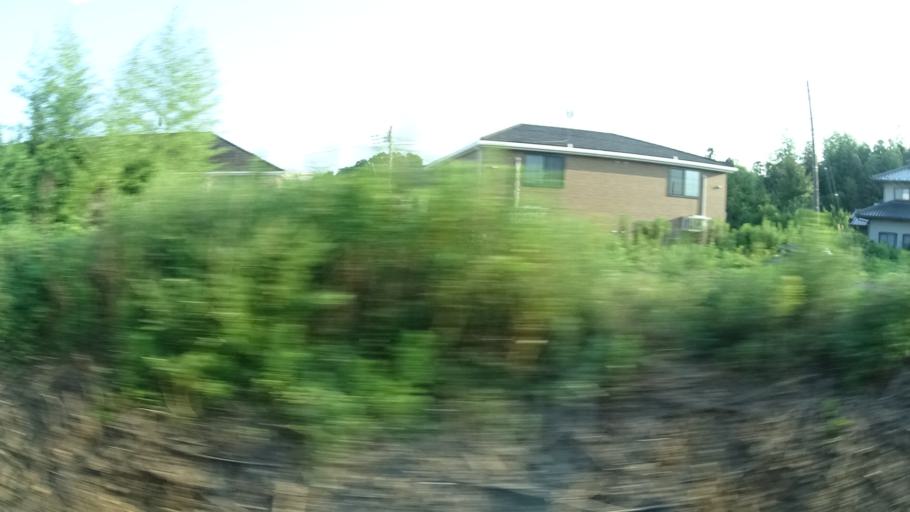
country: JP
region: Ibaraki
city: Mito-shi
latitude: 36.3843
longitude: 140.4389
